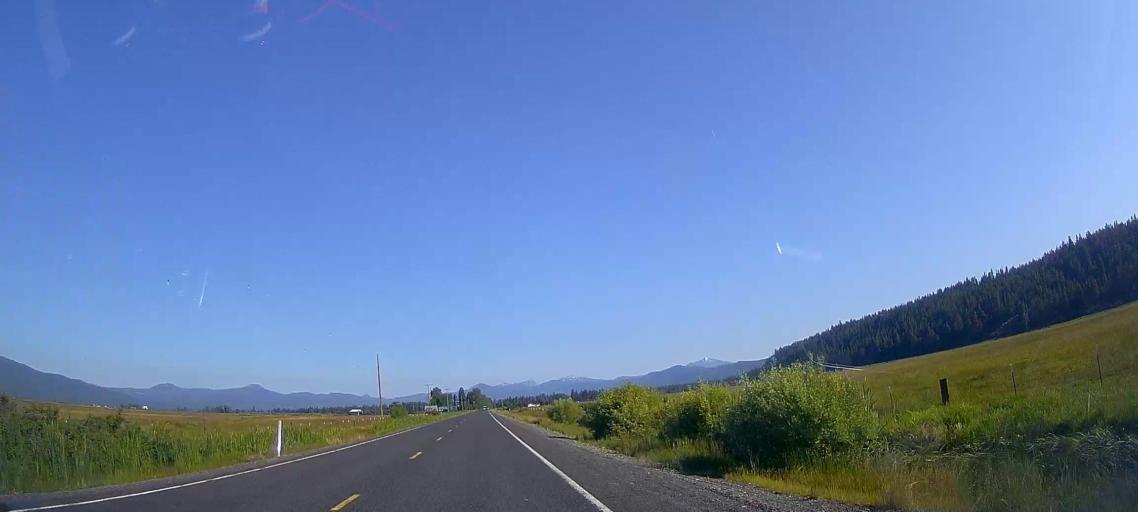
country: US
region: Oregon
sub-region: Klamath County
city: Klamath Falls
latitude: 42.6577
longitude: -121.9611
